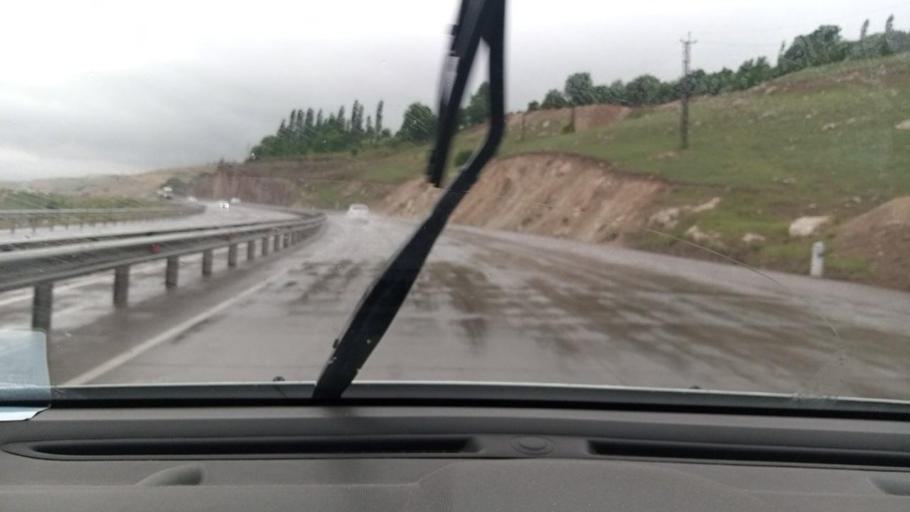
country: UZ
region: Toshkent
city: Angren
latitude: 41.0749
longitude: 70.2629
